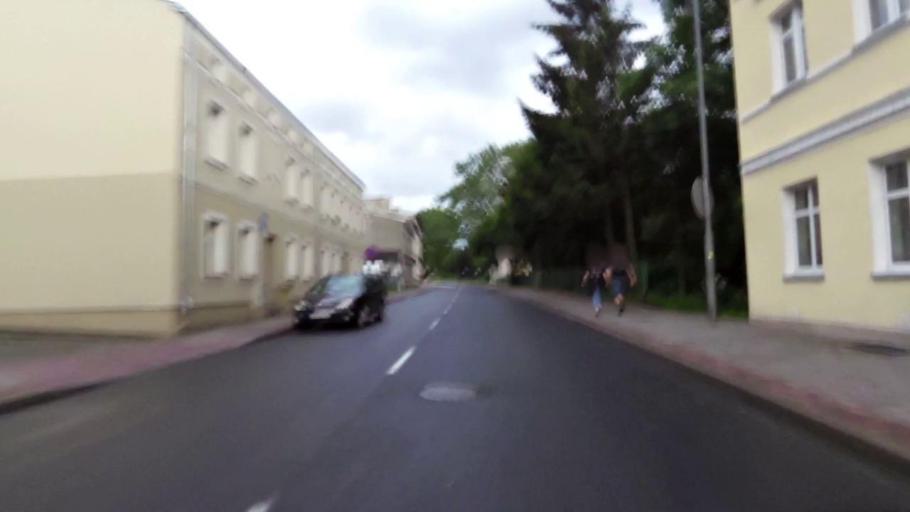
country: PL
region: West Pomeranian Voivodeship
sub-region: Koszalin
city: Koszalin
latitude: 54.1950
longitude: 16.1814
